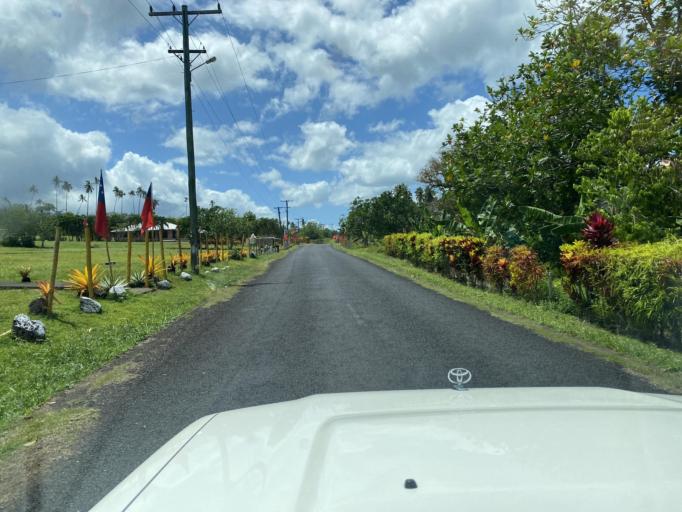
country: WS
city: Lotofaga
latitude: -14.0050
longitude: -171.7978
